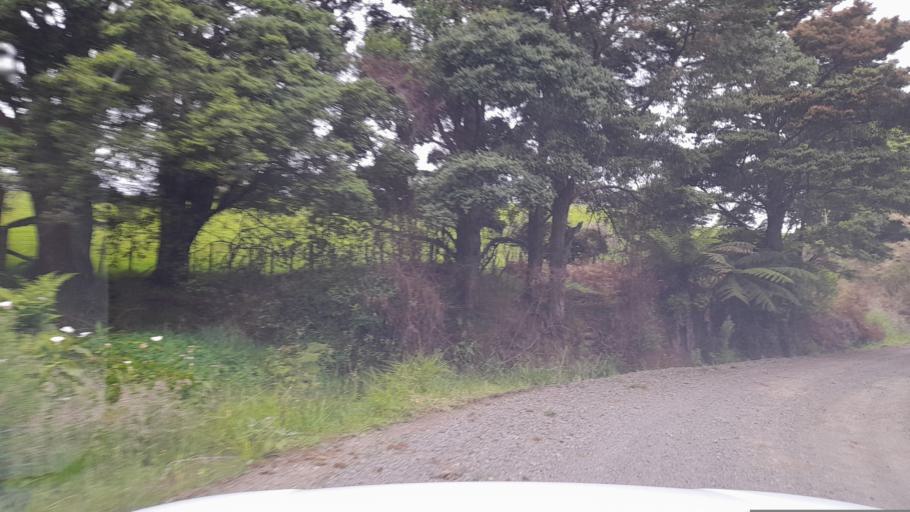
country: NZ
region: Northland
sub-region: Far North District
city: Waimate North
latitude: -35.3953
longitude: 173.7843
